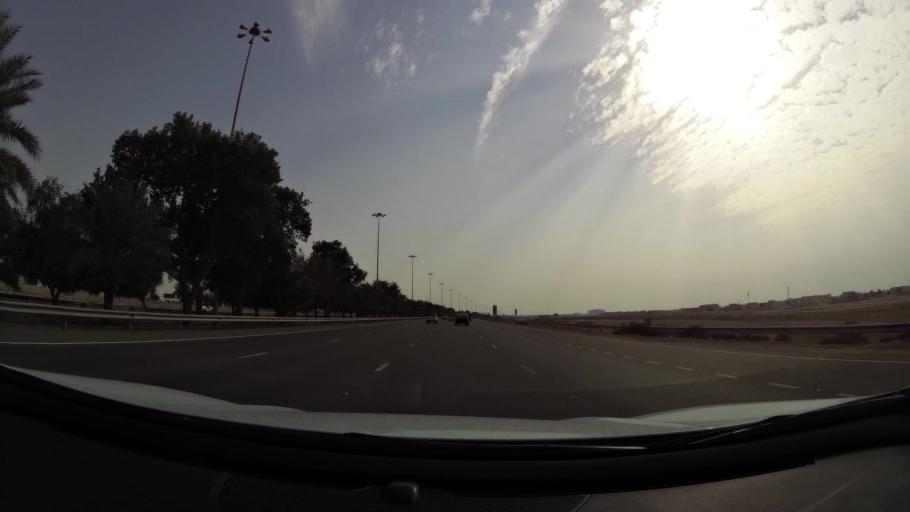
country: AE
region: Abu Dhabi
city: Abu Dhabi
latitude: 24.3653
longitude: 54.6522
